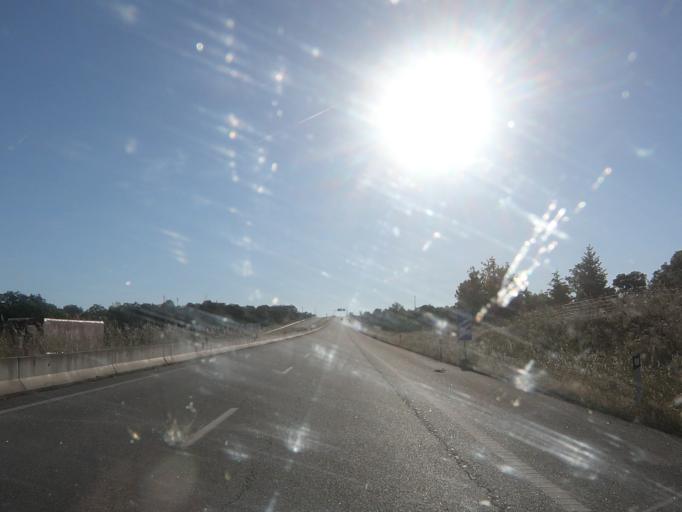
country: PT
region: Guarda
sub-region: Pinhel
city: Pinhel
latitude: 40.6039
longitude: -7.0540
